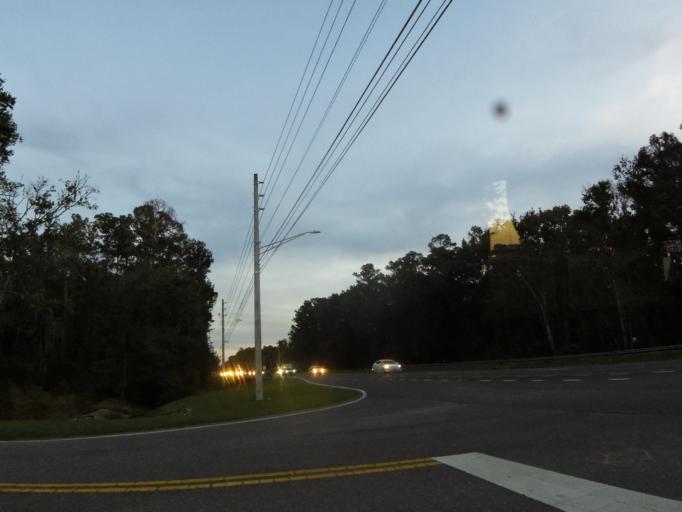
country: GA
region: Ogooue-Maritime
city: Port-Gentil
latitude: -0.3079
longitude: 7.9988
